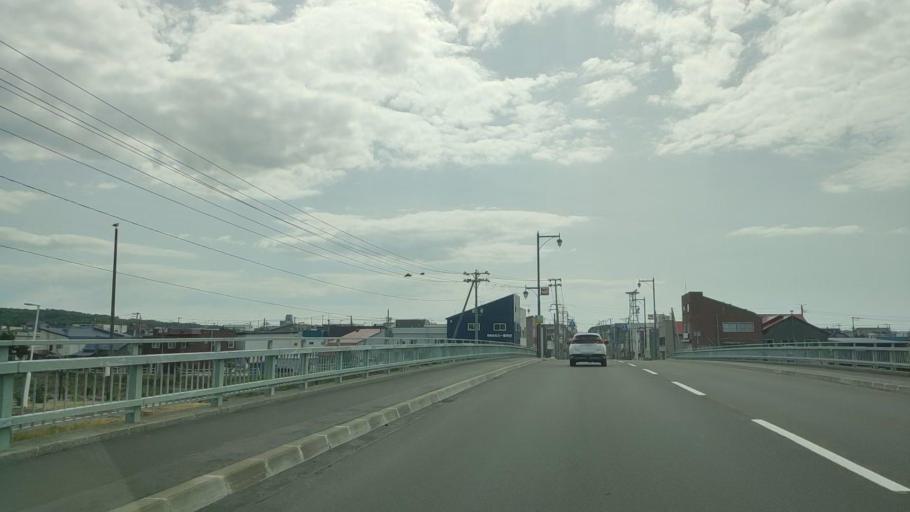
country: JP
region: Hokkaido
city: Rumoi
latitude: 44.3682
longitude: 141.7052
